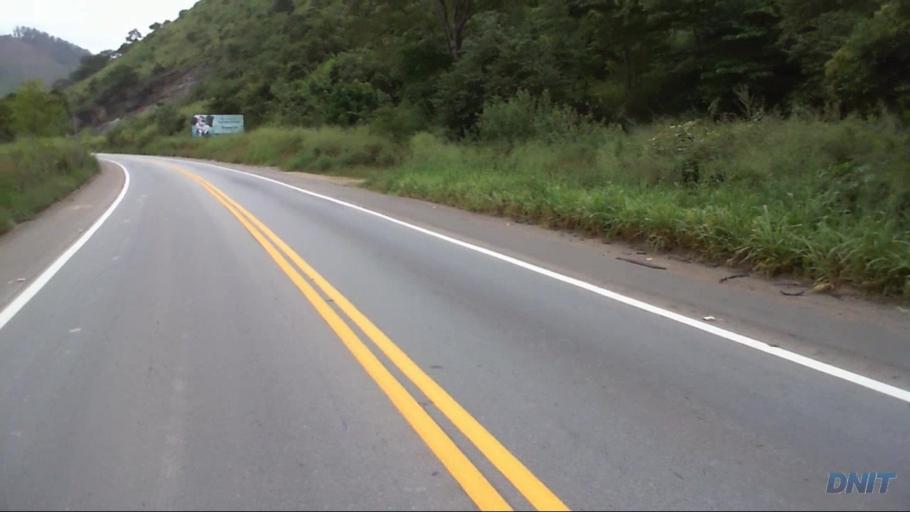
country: BR
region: Minas Gerais
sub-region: Timoteo
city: Timoteo
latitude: -19.5474
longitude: -42.6934
